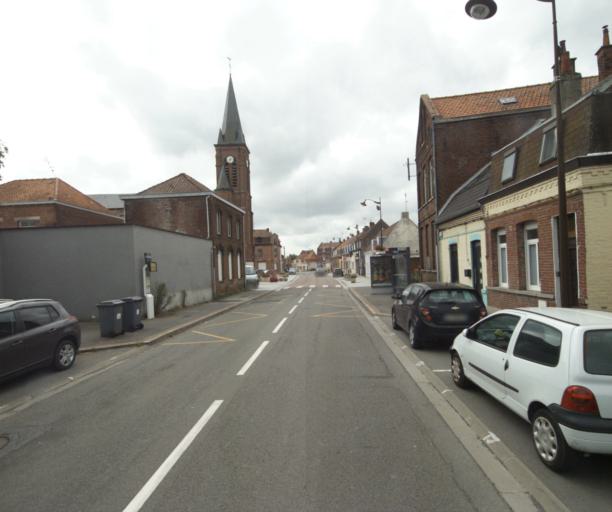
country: FR
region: Nord-Pas-de-Calais
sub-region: Departement du Nord
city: Forest-sur-Marque
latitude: 50.6364
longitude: 3.1891
